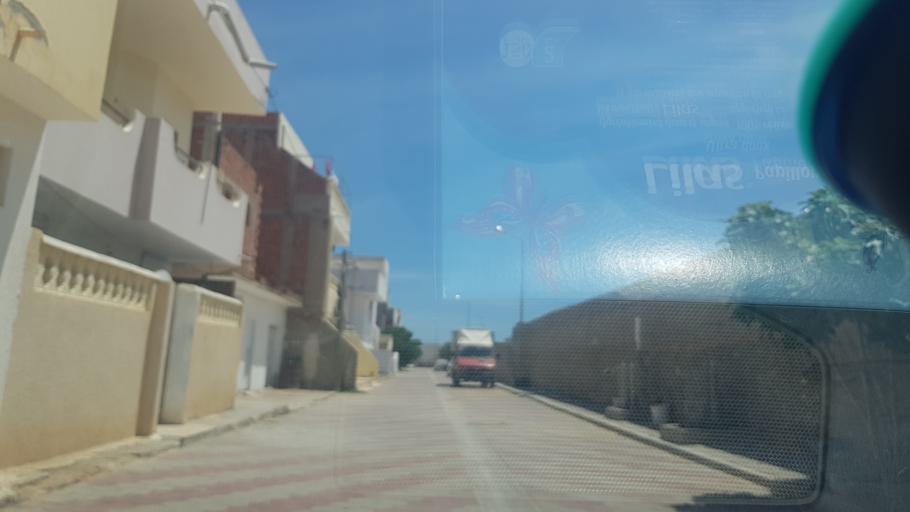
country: TN
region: Safaqis
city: Al Qarmadah
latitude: 34.8250
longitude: 10.7541
